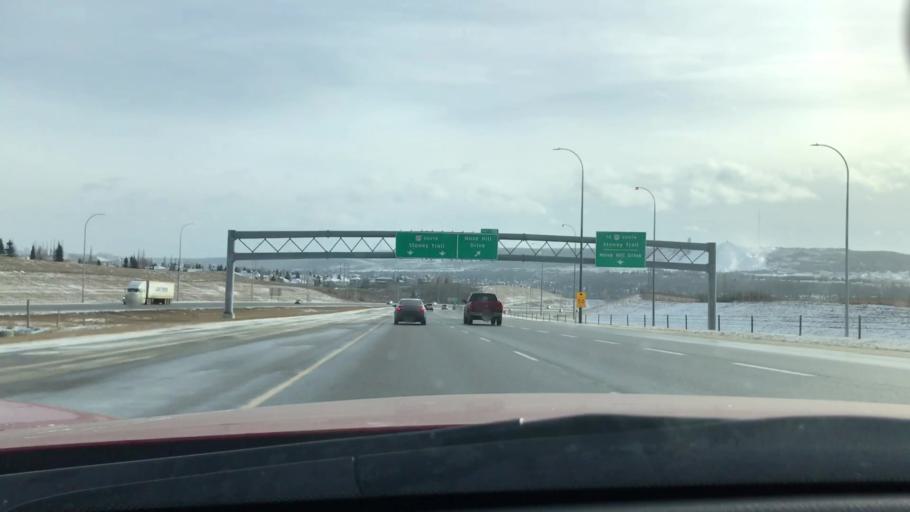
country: CA
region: Alberta
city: Calgary
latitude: 51.1138
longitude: -114.2276
